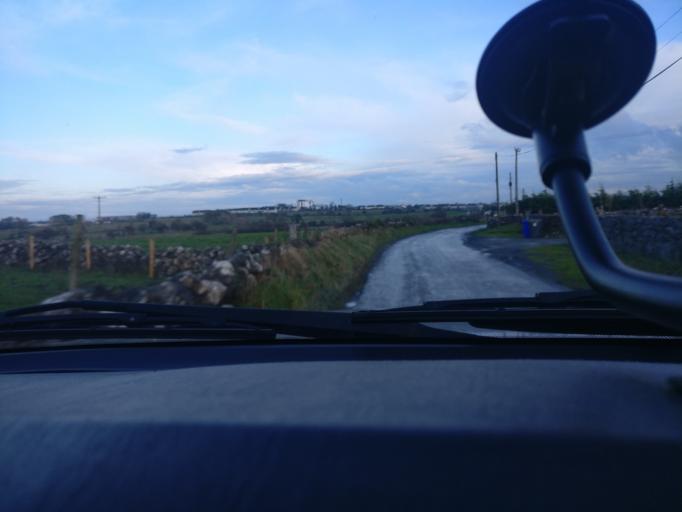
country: IE
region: Connaught
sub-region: County Galway
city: Loughrea
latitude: 53.1985
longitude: -8.6005
